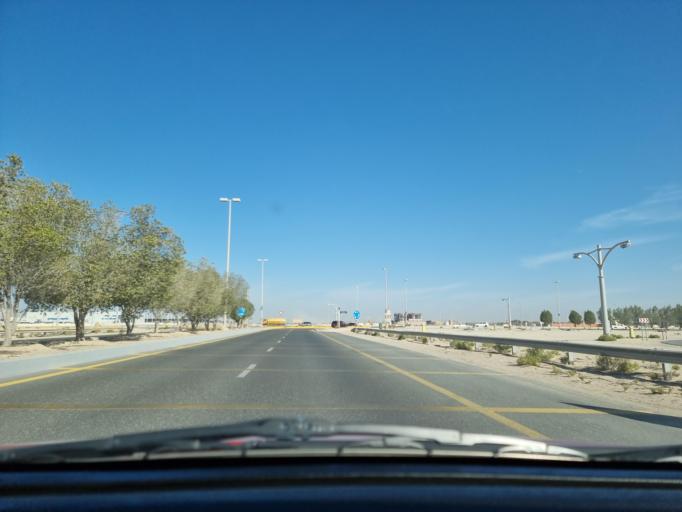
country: AE
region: Abu Dhabi
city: Abu Dhabi
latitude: 24.3965
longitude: 54.6938
